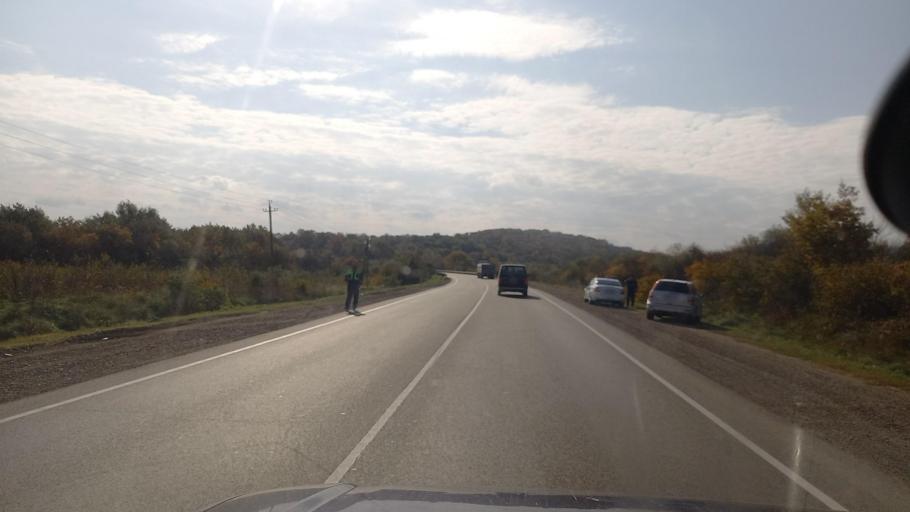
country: RU
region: Krasnodarskiy
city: Abinsk
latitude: 44.8536
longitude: 38.1341
